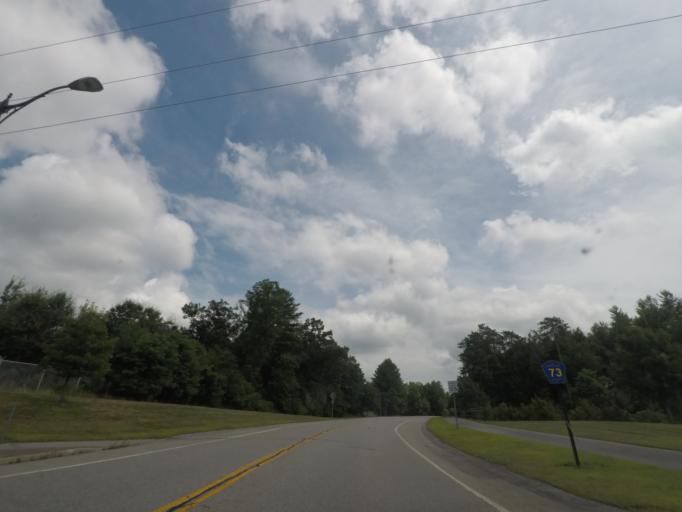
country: US
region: New York
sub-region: Saratoga County
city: Country Knolls
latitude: 42.9630
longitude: -73.7635
